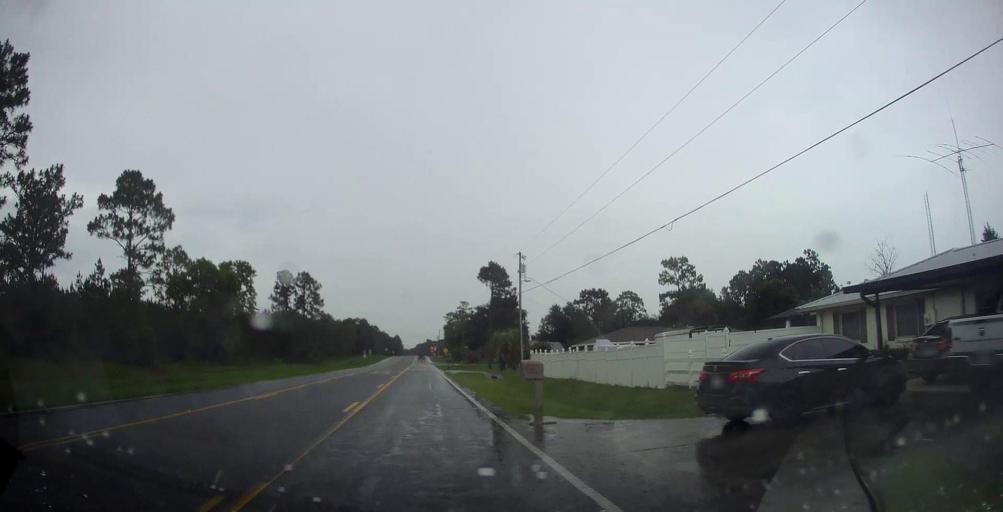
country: US
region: Florida
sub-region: Marion County
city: Silver Springs Shores
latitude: 29.1175
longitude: -82.0182
